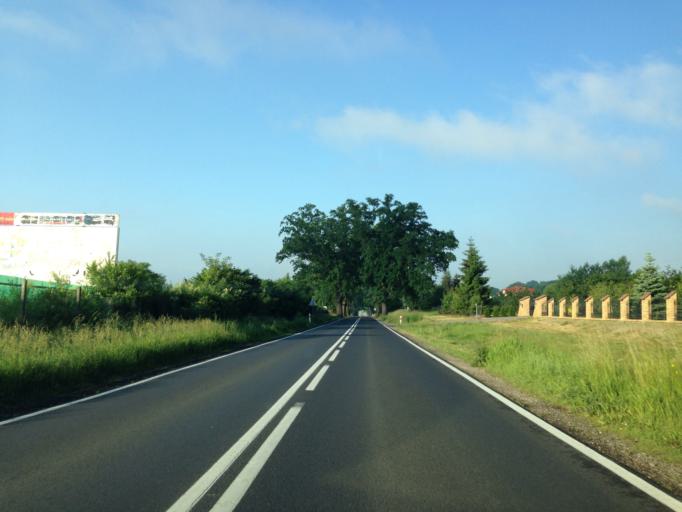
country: PL
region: Kujawsko-Pomorskie
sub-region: Grudziadz
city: Grudziadz
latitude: 53.5141
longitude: 18.8085
